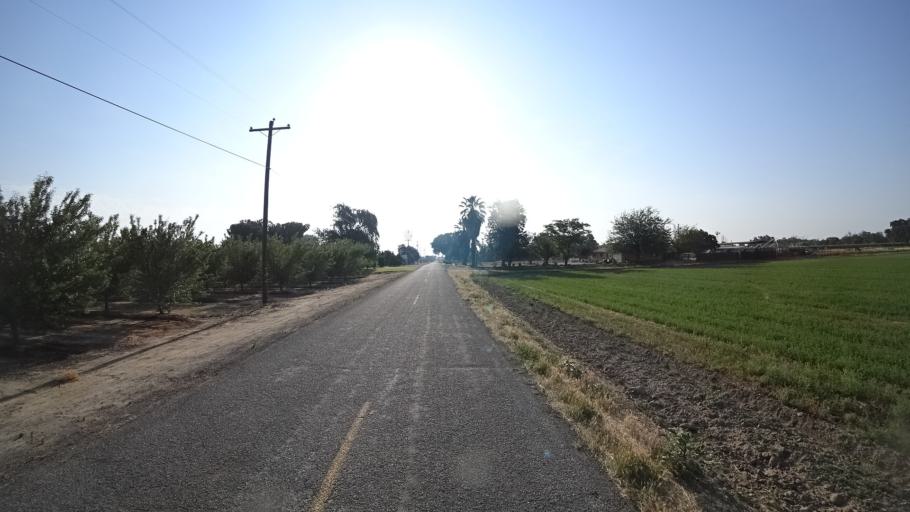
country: US
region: California
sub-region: Kings County
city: Lemoore
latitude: 36.3730
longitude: -119.8053
